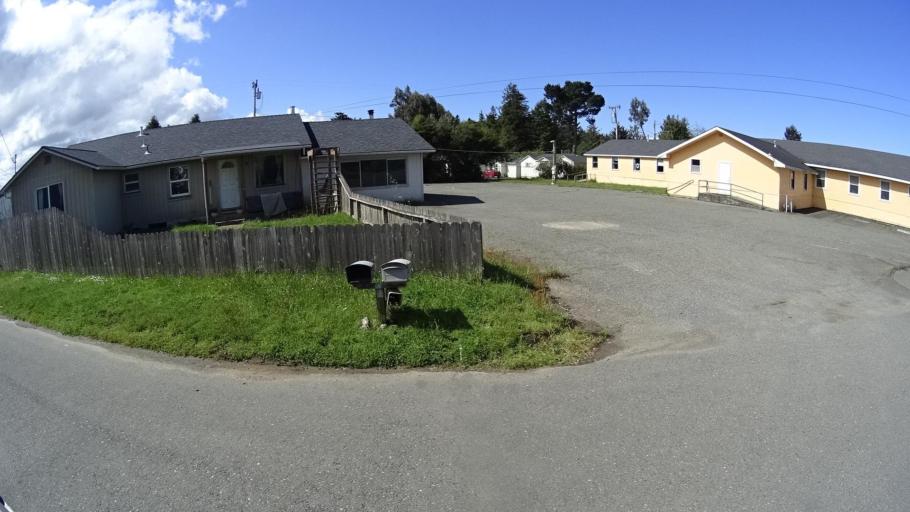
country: US
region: California
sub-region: Humboldt County
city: McKinleyville
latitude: 40.9356
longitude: -124.0908
